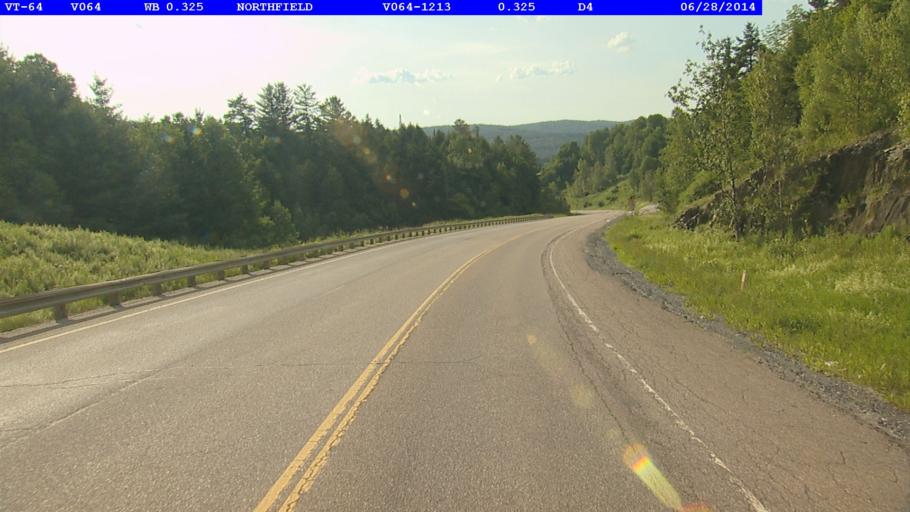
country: US
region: Vermont
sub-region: Washington County
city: Northfield
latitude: 44.1163
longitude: -72.6511
